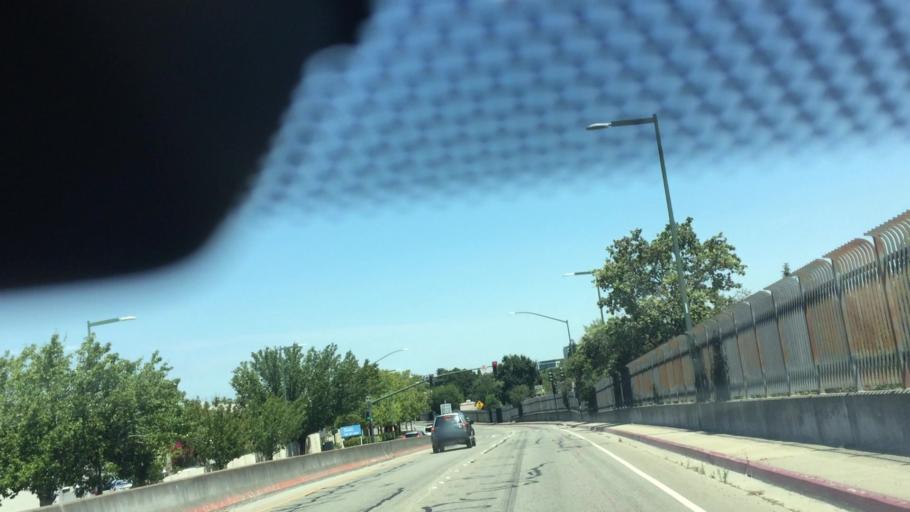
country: US
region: California
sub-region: Contra Costa County
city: Walnut Creek
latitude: 37.9123
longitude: -122.0642
